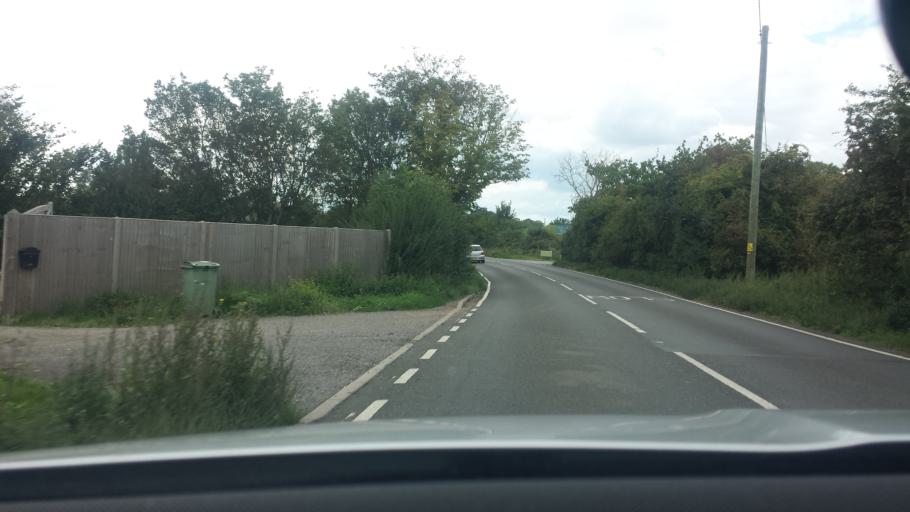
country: GB
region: England
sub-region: Kent
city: Staplehurst
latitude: 51.1973
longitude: 0.5283
